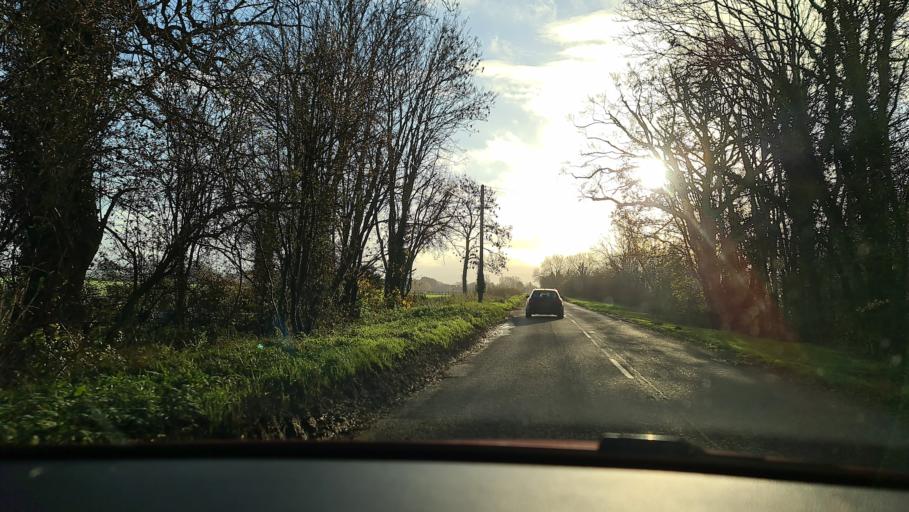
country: GB
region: England
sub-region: Buckinghamshire
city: Stone
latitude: 51.7925
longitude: -0.8467
